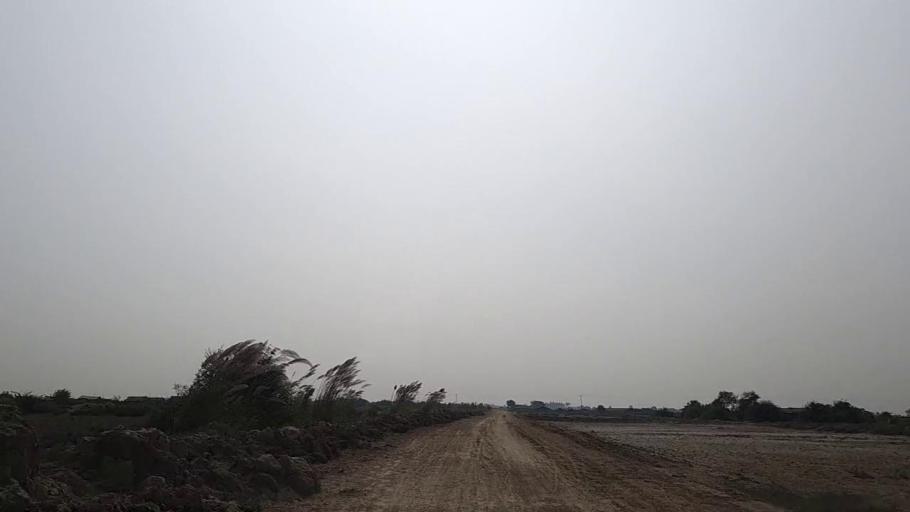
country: PK
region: Sindh
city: Mirpur Sakro
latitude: 24.6331
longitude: 67.7675
